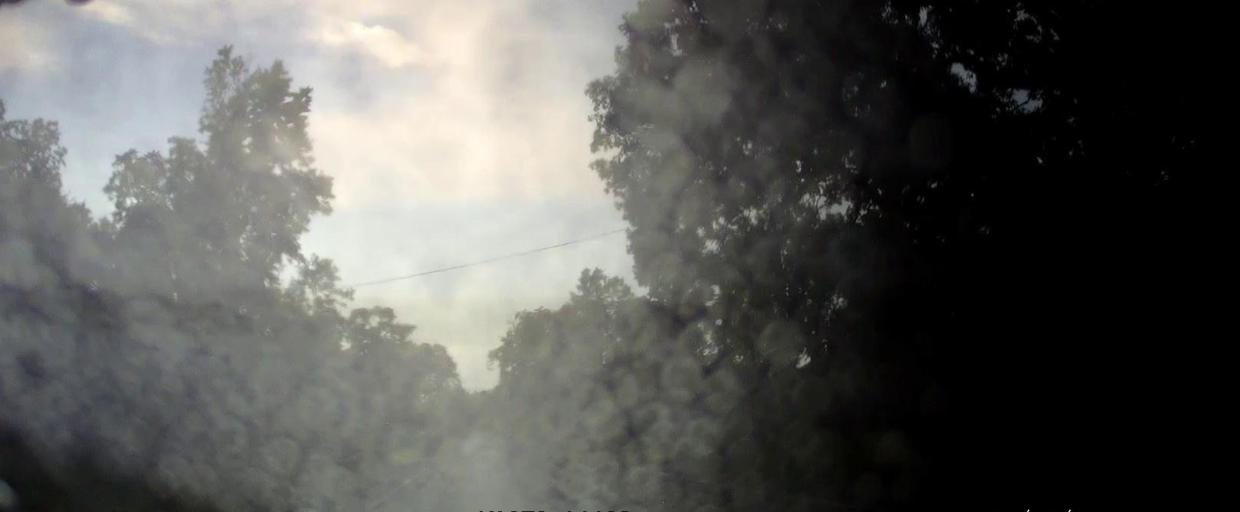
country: US
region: Georgia
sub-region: Dodge County
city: Chester
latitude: 32.5574
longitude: -83.1500
